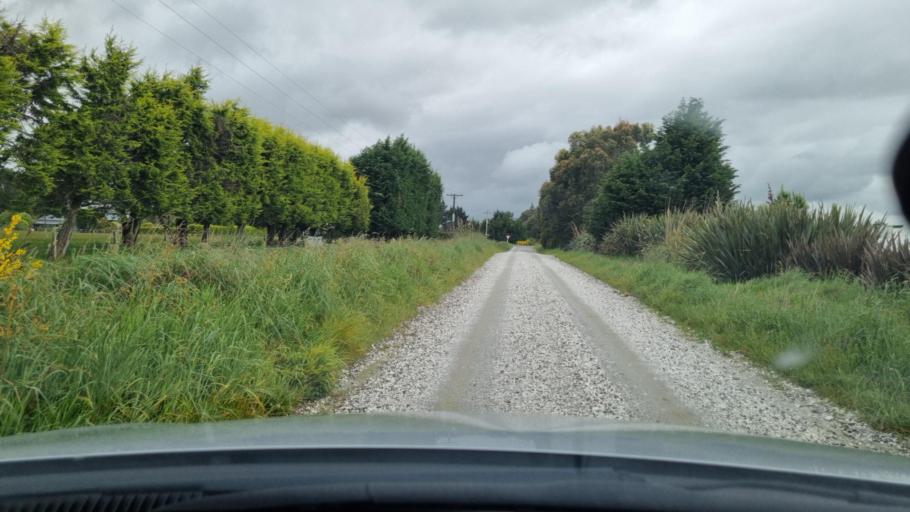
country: NZ
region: Southland
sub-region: Invercargill City
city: Invercargill
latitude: -46.4523
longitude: 168.3884
